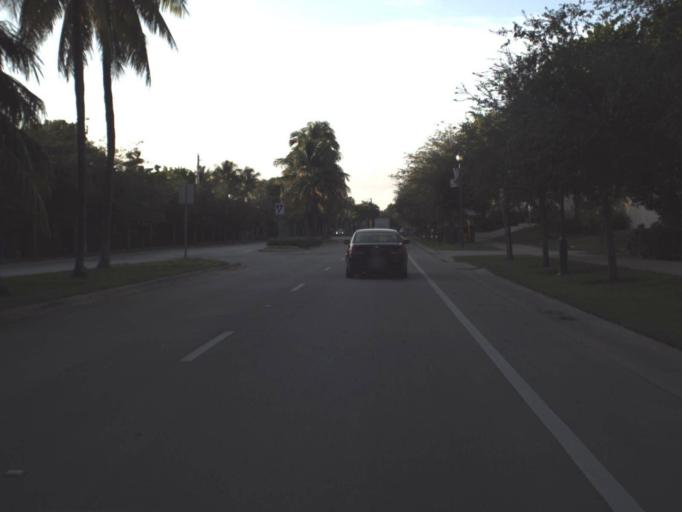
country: US
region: Florida
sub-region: Miami-Dade County
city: Key Biscayne
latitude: 25.6849
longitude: -80.1604
